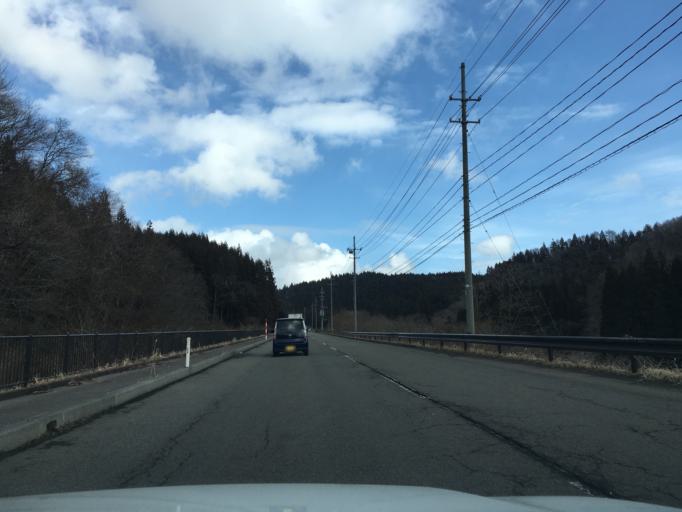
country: JP
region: Akita
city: Takanosu
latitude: 40.0905
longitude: 140.3366
